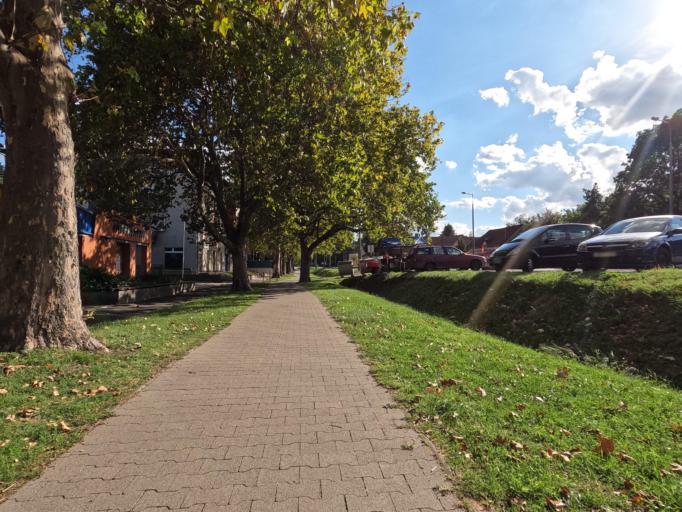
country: HU
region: Tolna
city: Paks
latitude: 46.6194
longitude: 18.8530
